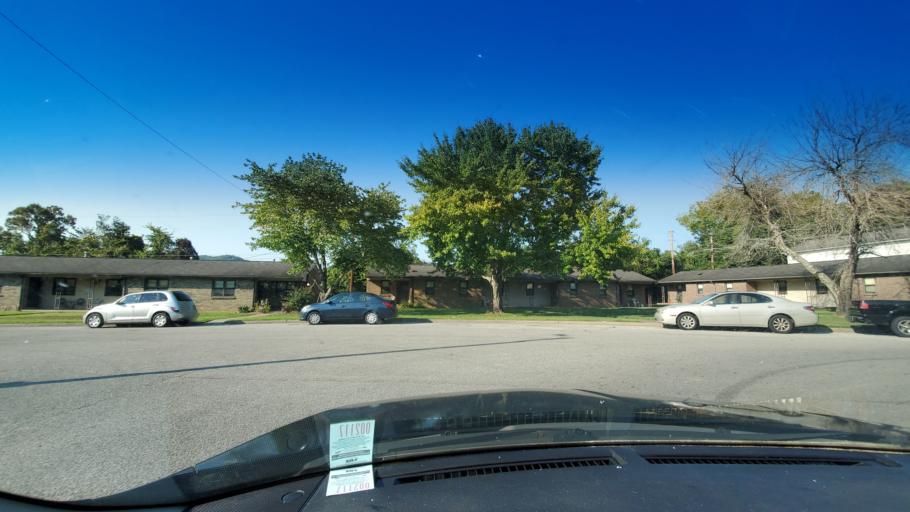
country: US
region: Tennessee
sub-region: Smith County
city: Carthage
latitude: 36.2561
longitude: -85.9544
